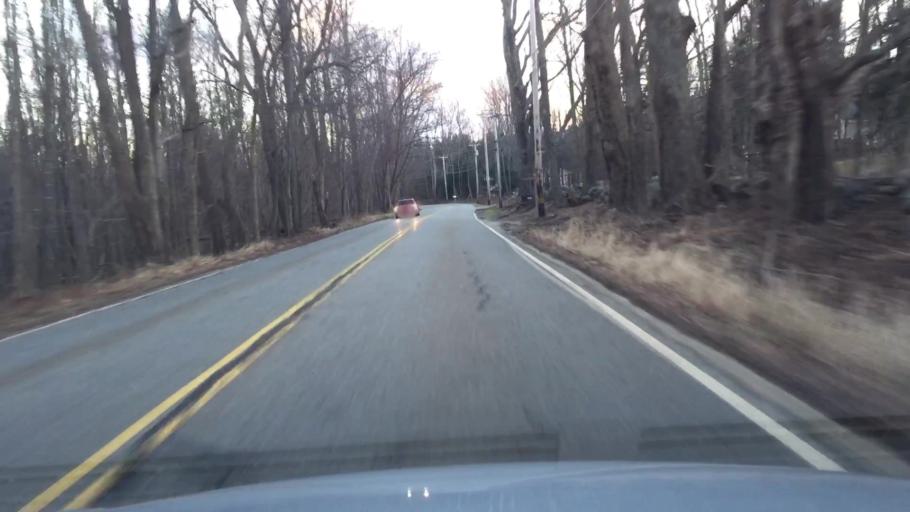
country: US
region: Massachusetts
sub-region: Worcester County
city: Princeton
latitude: 42.4434
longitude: -71.8349
